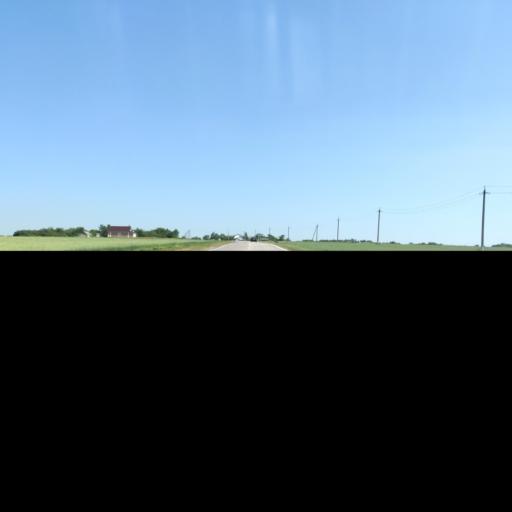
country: RU
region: Voronezj
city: Verkhnyaya Khava
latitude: 51.6867
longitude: 39.9333
